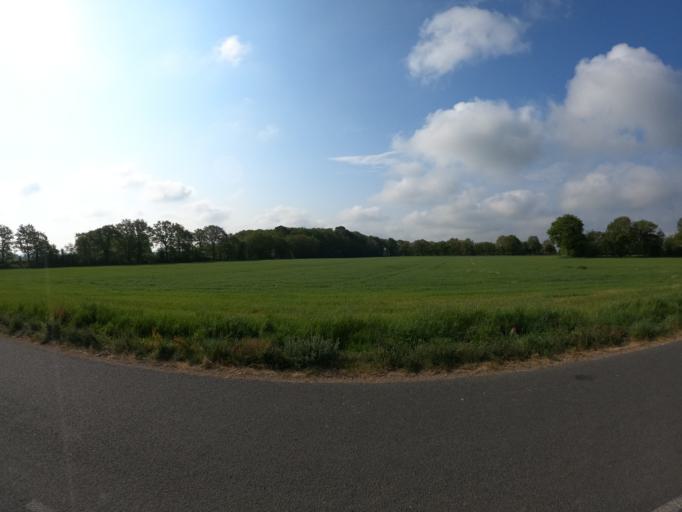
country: FR
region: Pays de la Loire
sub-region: Departement de Maine-et-Loire
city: La Romagne
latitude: 47.0644
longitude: -1.0391
